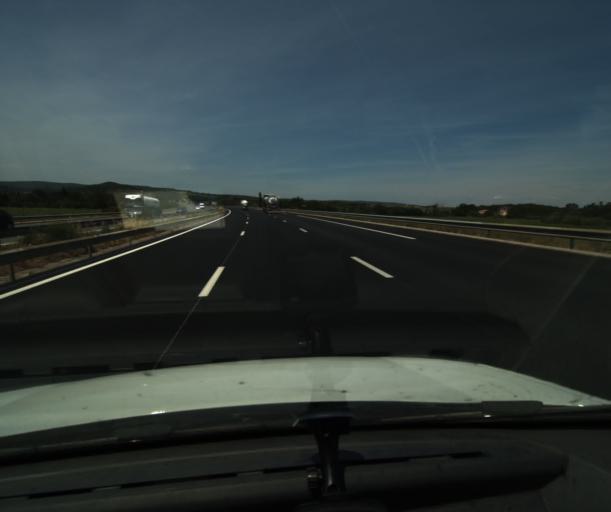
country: FR
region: Languedoc-Roussillon
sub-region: Departement de l'Aude
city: Sigean
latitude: 43.0399
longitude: 2.9508
